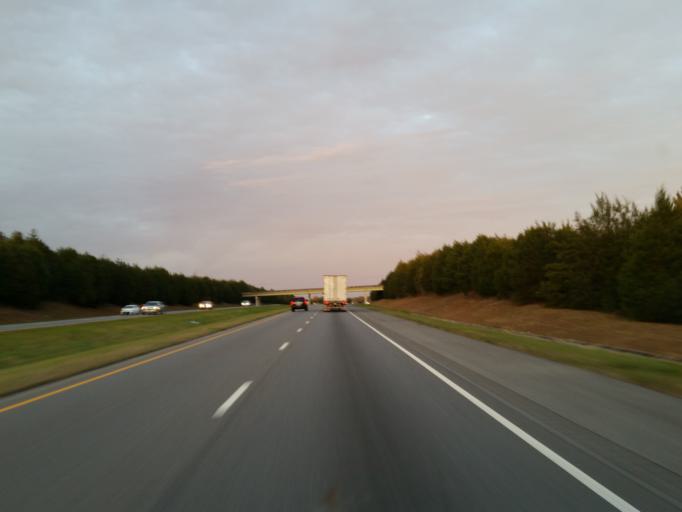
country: US
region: Alabama
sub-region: Sumter County
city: Livingston
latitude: 32.6779
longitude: -88.1663
